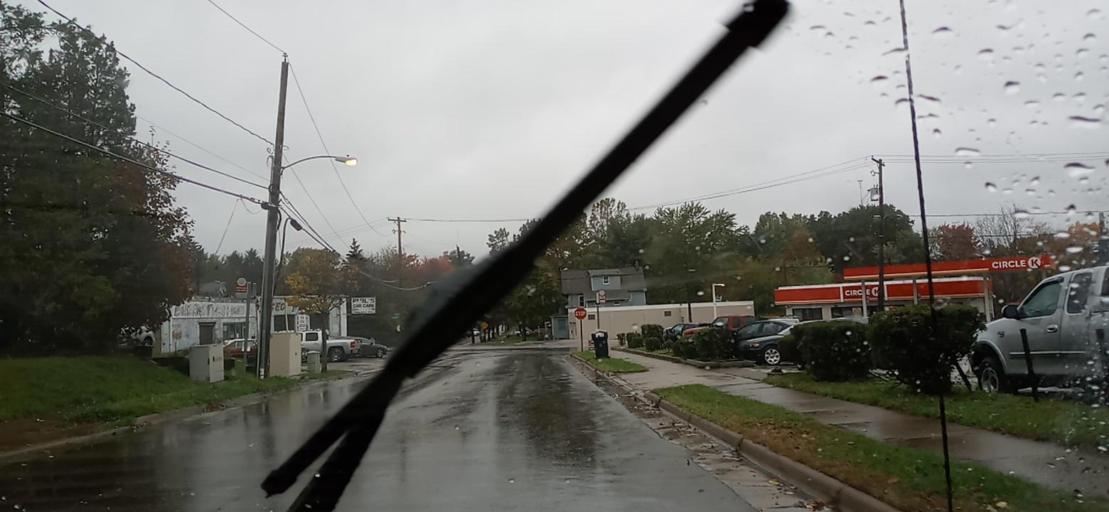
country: US
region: Ohio
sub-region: Summit County
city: Akron
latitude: 41.0573
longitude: -81.5595
